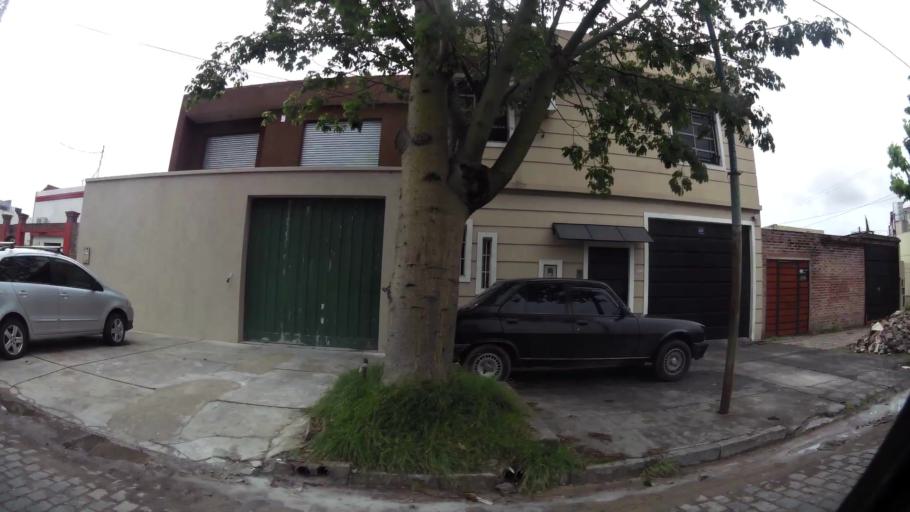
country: AR
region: Buenos Aires
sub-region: Partido de Lanus
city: Lanus
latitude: -34.7340
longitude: -58.3857
